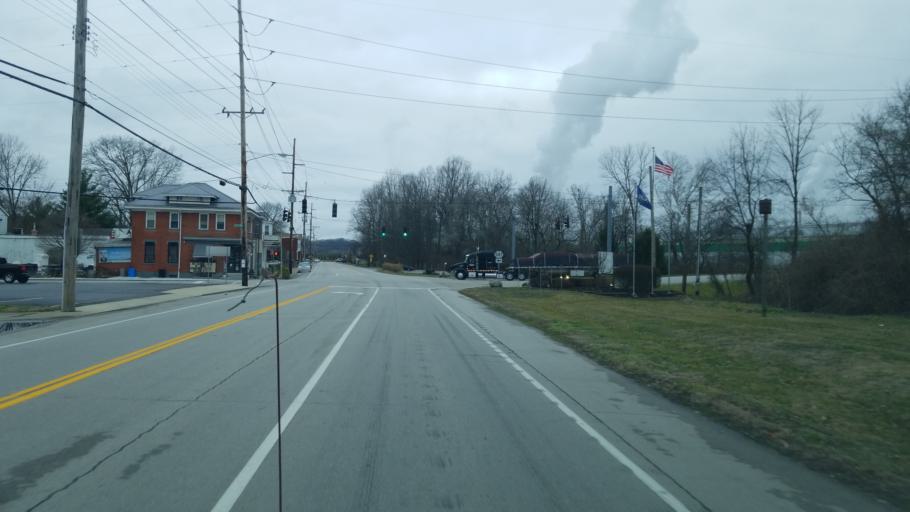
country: US
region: Kentucky
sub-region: Campbell County
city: Silver Grove
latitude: 39.0363
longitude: -84.3887
